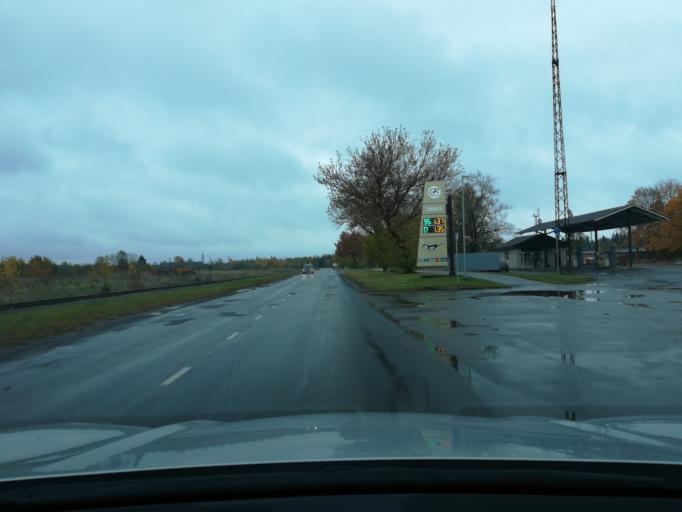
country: EE
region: Ida-Virumaa
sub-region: Johvi vald
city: Johvi
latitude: 59.3201
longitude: 27.4279
